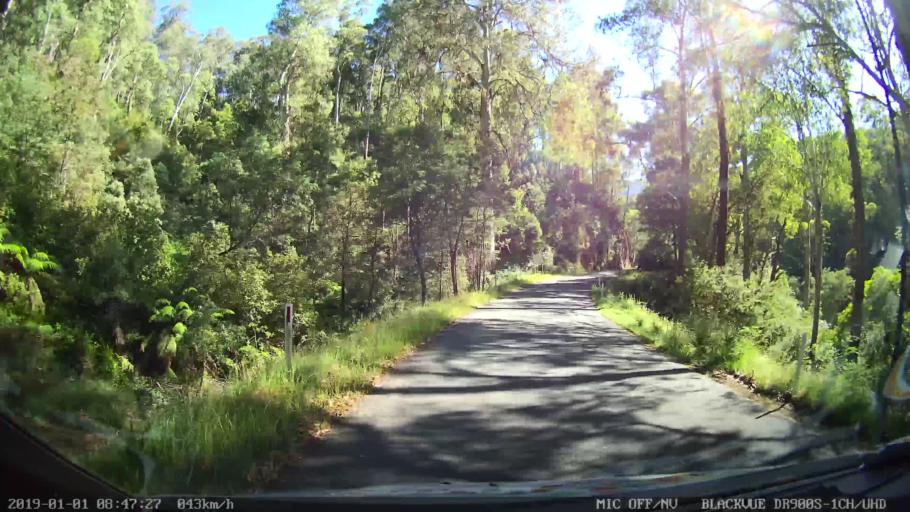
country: AU
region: New South Wales
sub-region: Snowy River
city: Jindabyne
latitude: -36.2941
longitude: 148.1971
